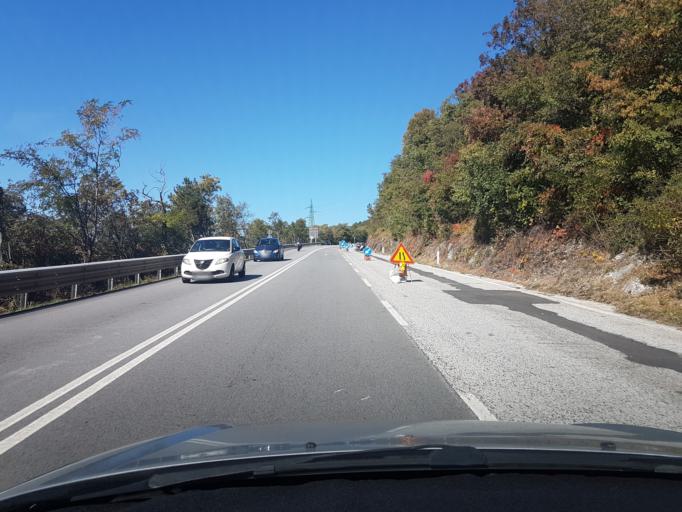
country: IT
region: Friuli Venezia Giulia
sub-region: Provincia di Trieste
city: Domio
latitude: 45.6372
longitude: 13.8360
